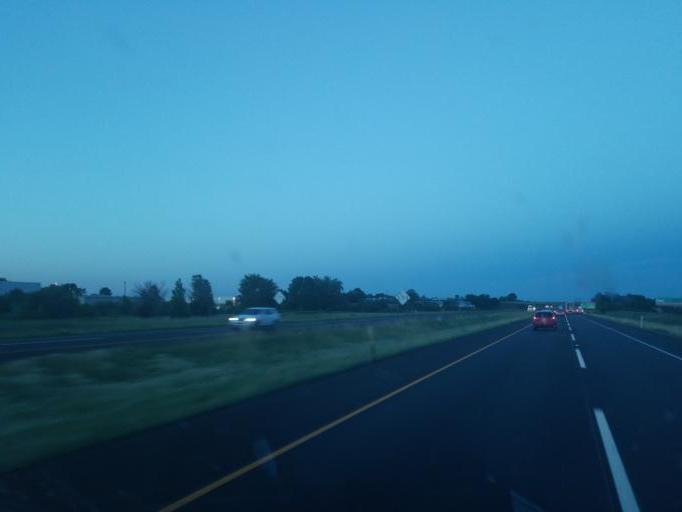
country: US
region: Michigan
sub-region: Berrien County
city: Buchanan
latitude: 41.7303
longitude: -86.3465
